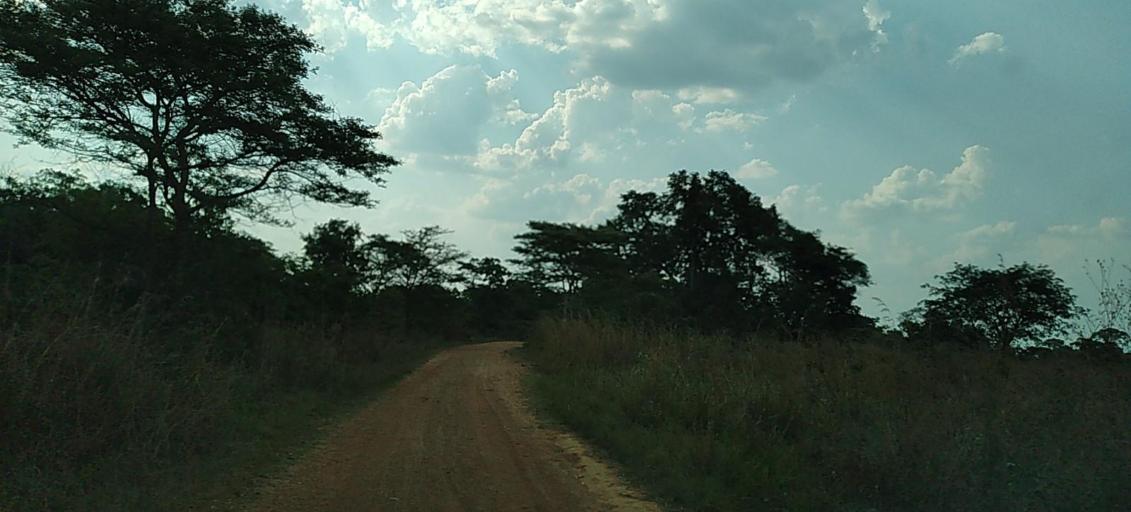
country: ZM
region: Copperbelt
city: Mpongwe
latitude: -13.5113
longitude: 28.0951
